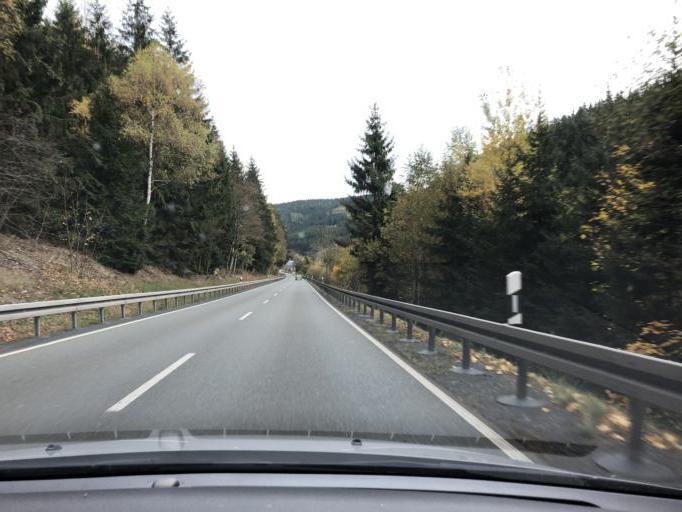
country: DE
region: Thuringia
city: Lichte
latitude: 50.5206
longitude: 11.1623
